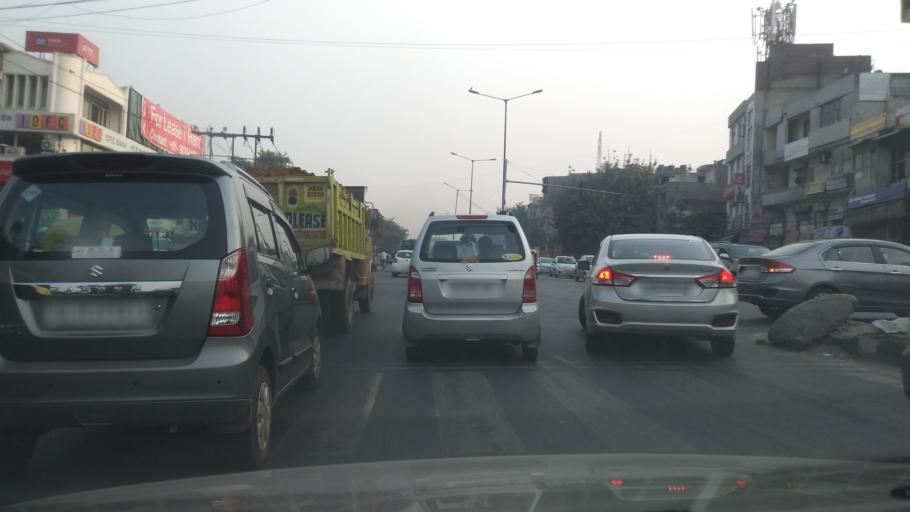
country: IN
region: Uttar Pradesh
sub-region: Gautam Buddha Nagar
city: Noida
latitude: 28.5371
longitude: 77.2674
